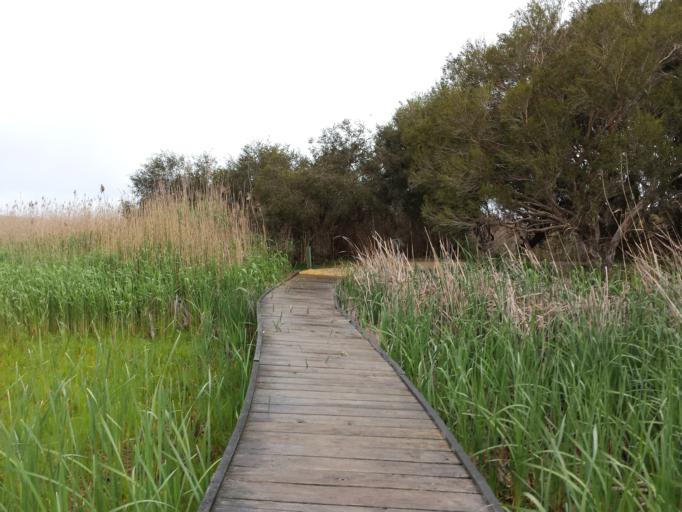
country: AU
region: South Australia
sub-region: Naracoorte and Lucindale
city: Naracoorte
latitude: -37.1021
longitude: 140.7175
